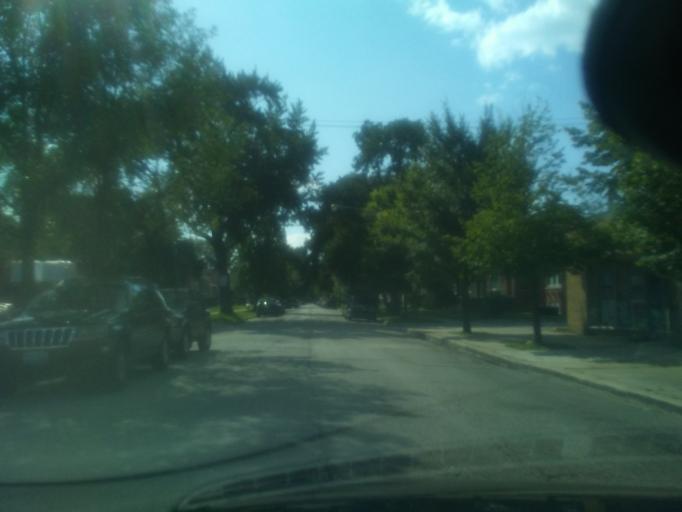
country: US
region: Illinois
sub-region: Cook County
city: Harwood Heights
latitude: 41.9596
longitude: -87.7675
